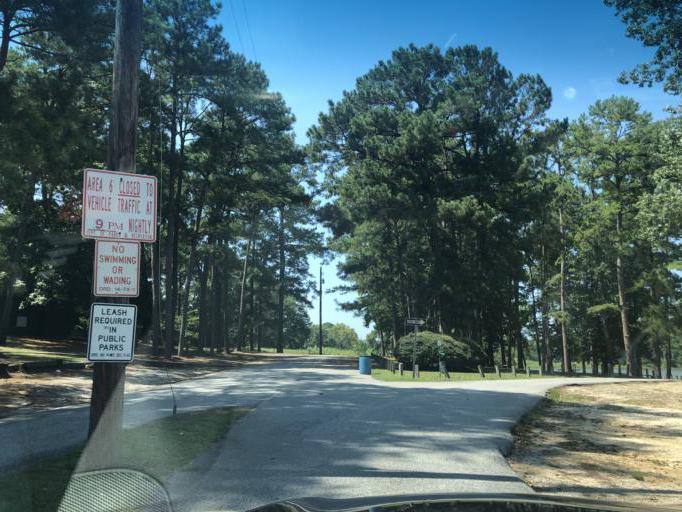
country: US
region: Georgia
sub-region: Muscogee County
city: Columbus
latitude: 32.5091
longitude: -84.9139
